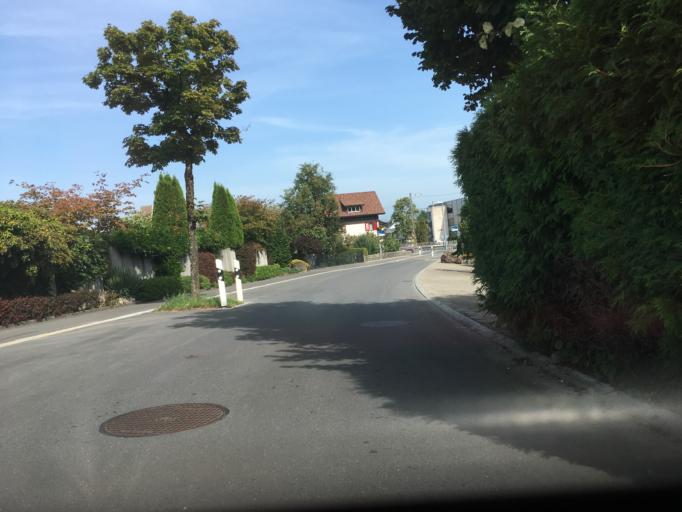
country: CH
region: Schwyz
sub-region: Bezirk Hoefe
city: Freienbach
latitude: 47.2035
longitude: 8.7561
